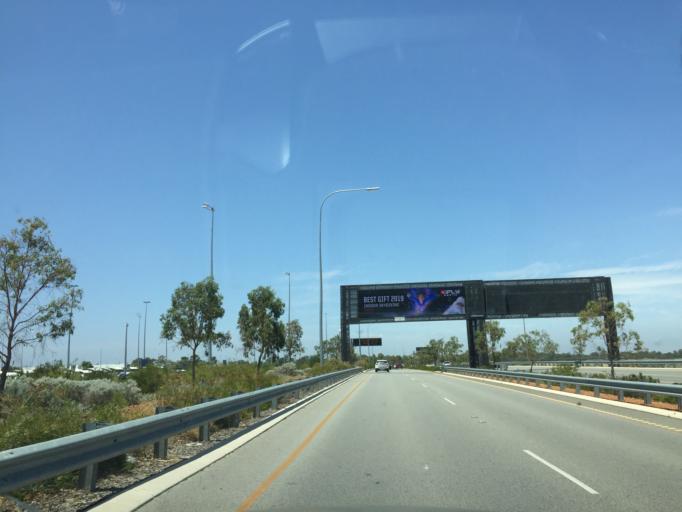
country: AU
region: Western Australia
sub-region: Belmont
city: Redcliffe
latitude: -31.9517
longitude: 115.9702
